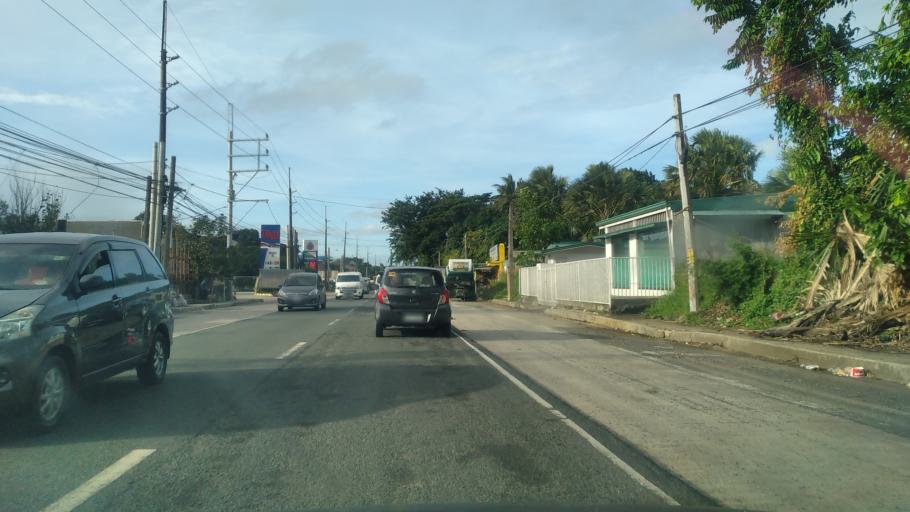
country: PH
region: Calabarzon
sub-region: Province of Quezon
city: Calumpang
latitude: 13.9742
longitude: 121.5551
